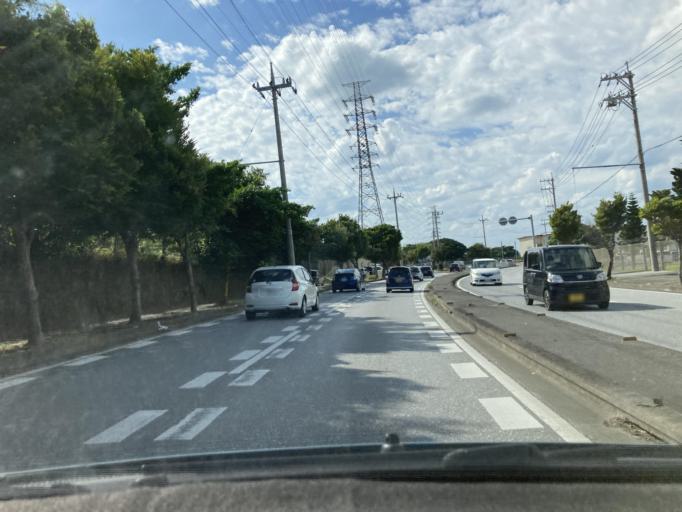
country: JP
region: Okinawa
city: Chatan
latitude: 26.3056
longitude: 127.7745
